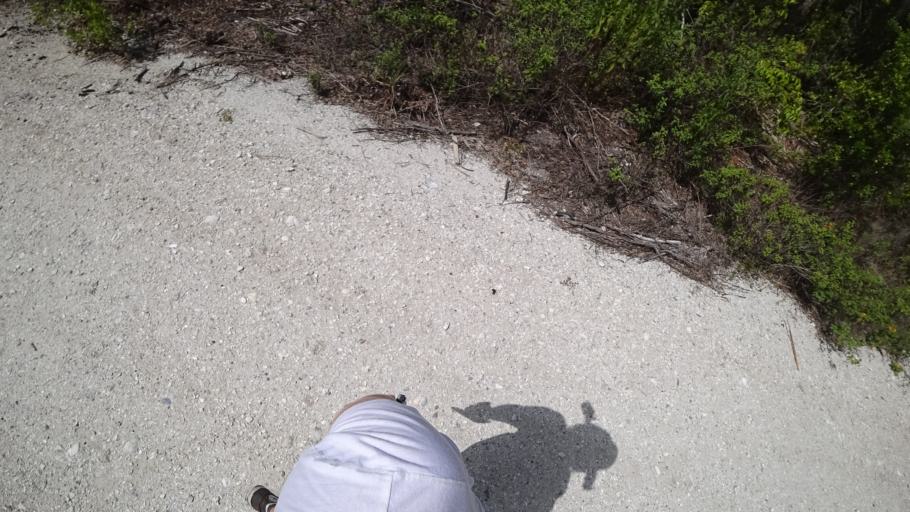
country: US
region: Florida
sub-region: Manatee County
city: Holmes Beach
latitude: 27.4948
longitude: -82.6857
